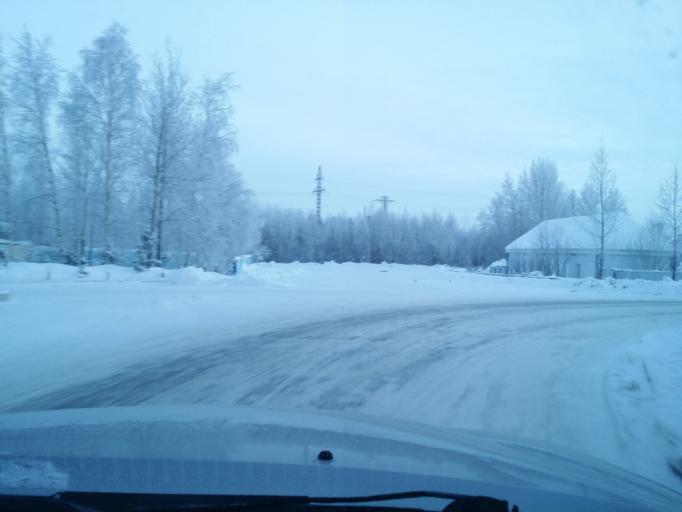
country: RU
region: Khanty-Mansiyskiy Avtonomnyy Okrug
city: Nizhnevartovsk
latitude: 60.9516
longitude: 76.5010
